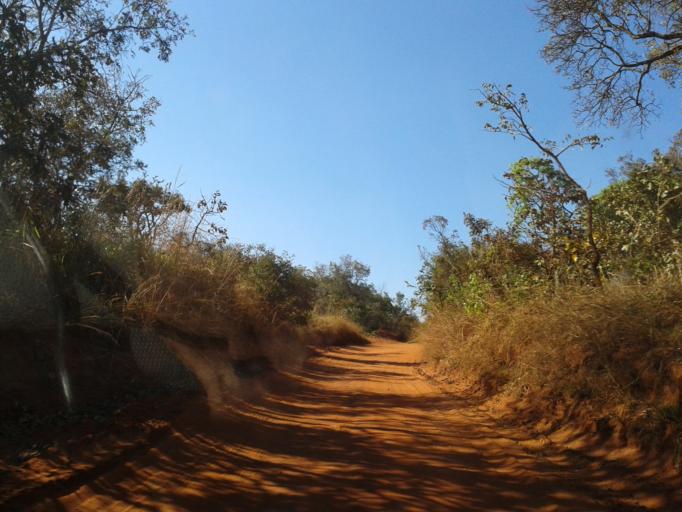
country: BR
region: Minas Gerais
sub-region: Ituiutaba
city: Ituiutaba
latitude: -19.0240
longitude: -49.3500
